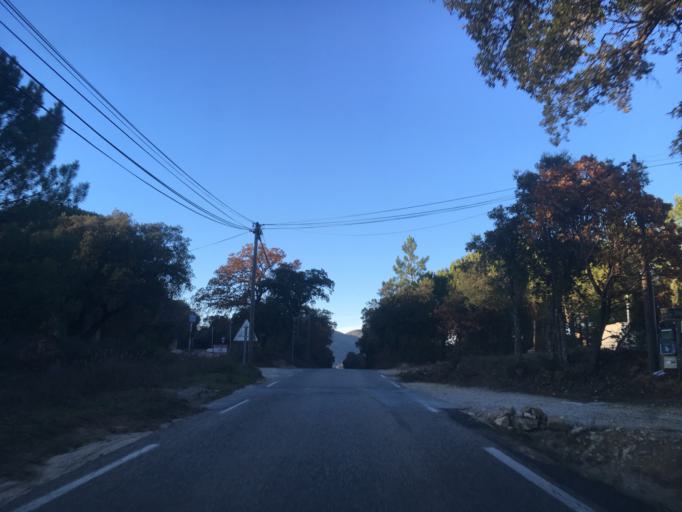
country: FR
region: Provence-Alpes-Cote d'Azur
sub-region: Departement du Var
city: Le Plan-de-la-Tour
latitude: 43.3104
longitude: 6.5507
